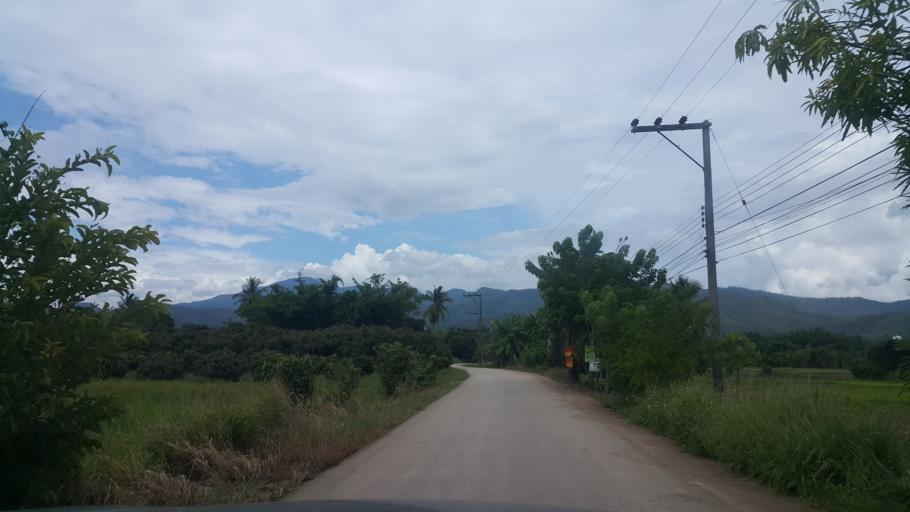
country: TH
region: Chiang Mai
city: Mae Taeng
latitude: 19.1933
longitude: 98.9991
